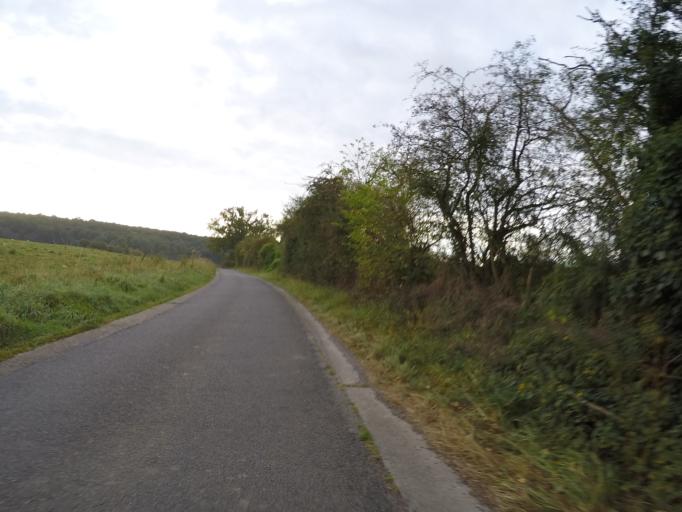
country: BE
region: Wallonia
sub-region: Province de Namur
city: Ciney
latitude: 50.3245
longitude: 5.0685
